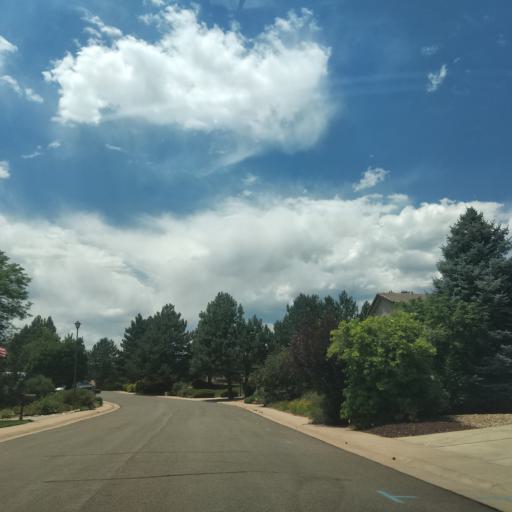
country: US
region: Colorado
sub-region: Jefferson County
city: Lakewood
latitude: 39.6746
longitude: -105.0942
